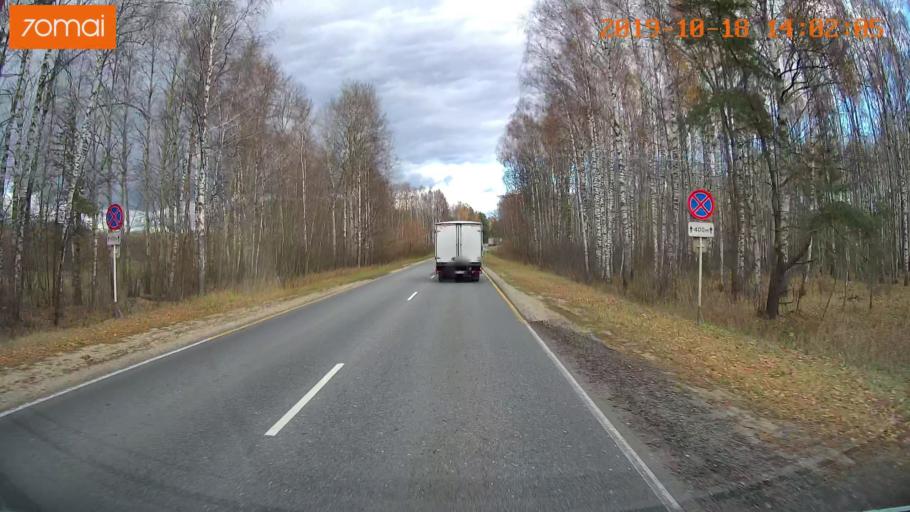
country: RU
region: Rjazan
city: Spas-Klepiki
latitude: 55.1112
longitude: 40.1011
